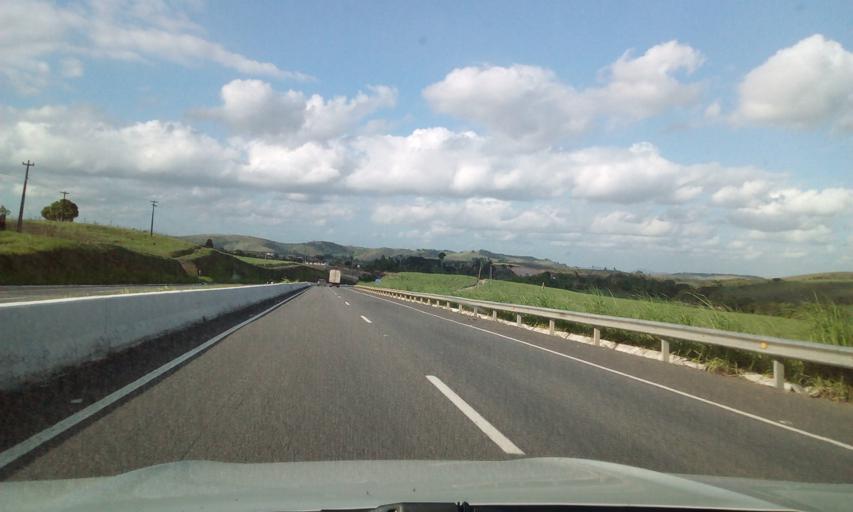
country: BR
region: Pernambuco
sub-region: Ribeirao
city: Ribeirao
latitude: -8.4723
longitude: -35.3712
